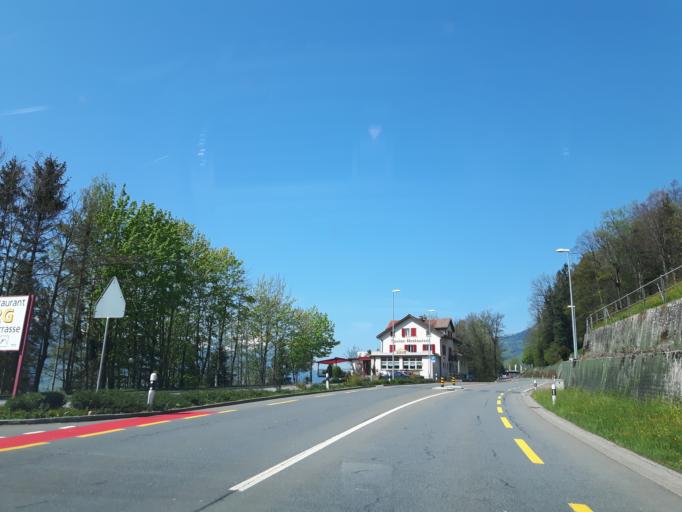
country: CH
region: Schwyz
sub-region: Bezirk Schwyz
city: Steinen
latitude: 47.0454
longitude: 8.6330
